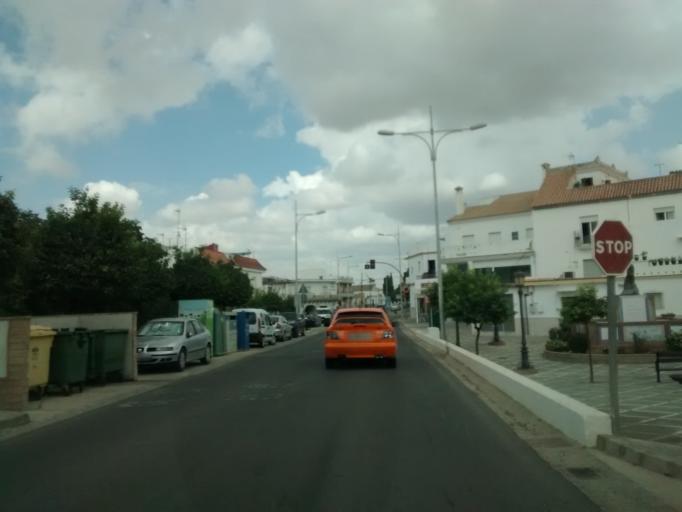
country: ES
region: Andalusia
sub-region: Provincia de Cadiz
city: Paterna de Rivera
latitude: 36.5216
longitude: -5.8676
